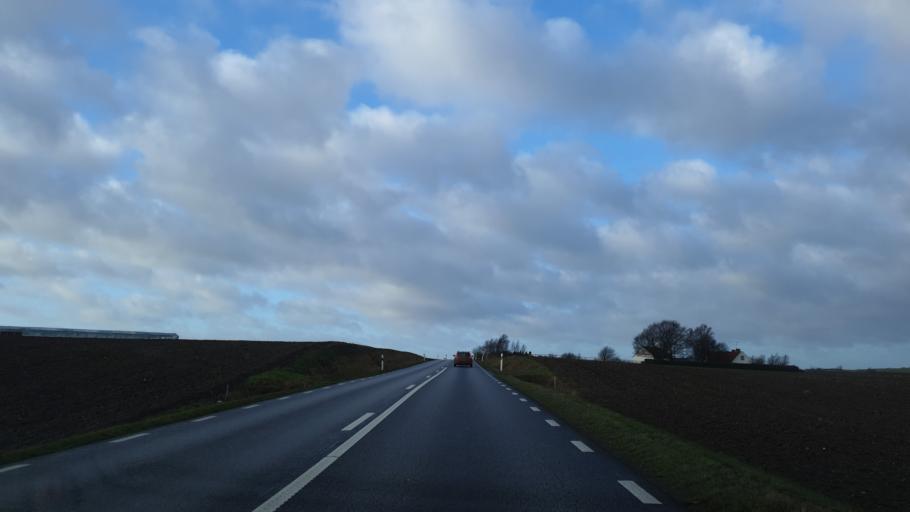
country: SE
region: Skane
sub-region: Trelleborgs Kommun
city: Trelleborg
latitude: 55.4566
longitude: 13.1687
